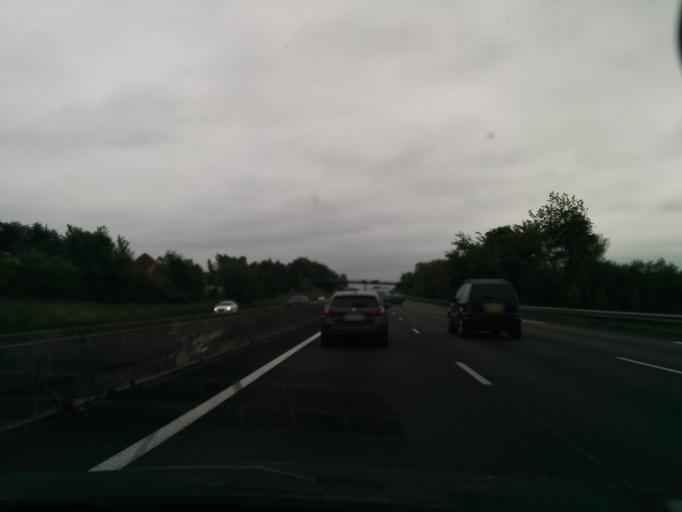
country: FR
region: Ile-de-France
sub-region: Departement des Yvelines
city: Orgeval
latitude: 48.9338
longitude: 1.9697
